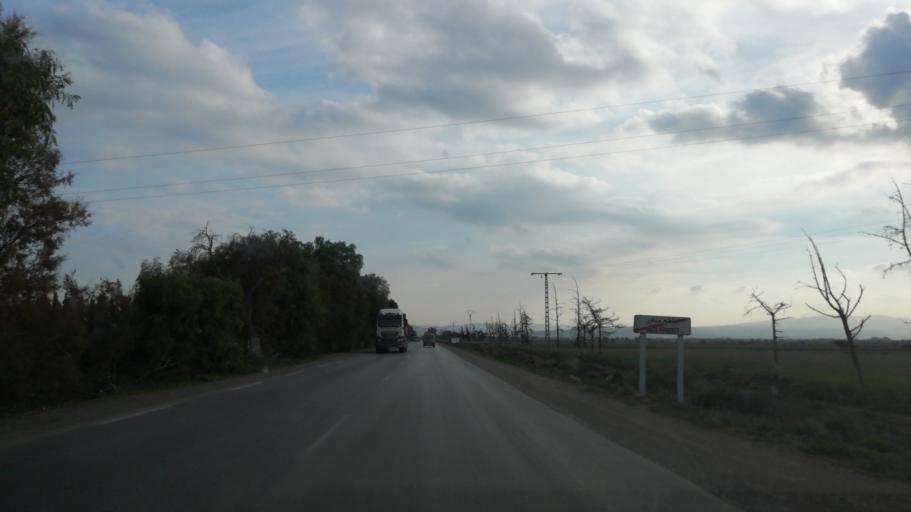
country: DZ
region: Mascara
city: Mascara
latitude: 35.6534
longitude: 0.0593
